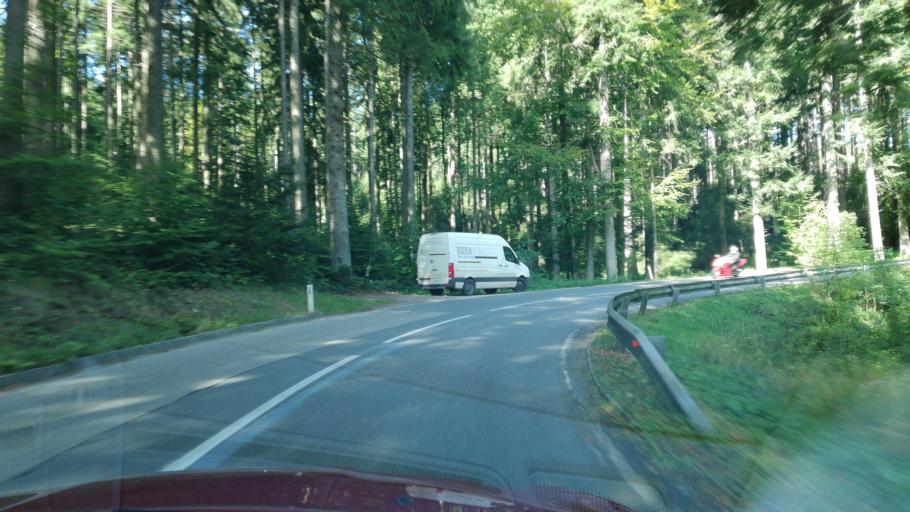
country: AT
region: Upper Austria
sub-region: Politischer Bezirk Vocklabruck
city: Redleiten
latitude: 48.1087
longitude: 13.5641
